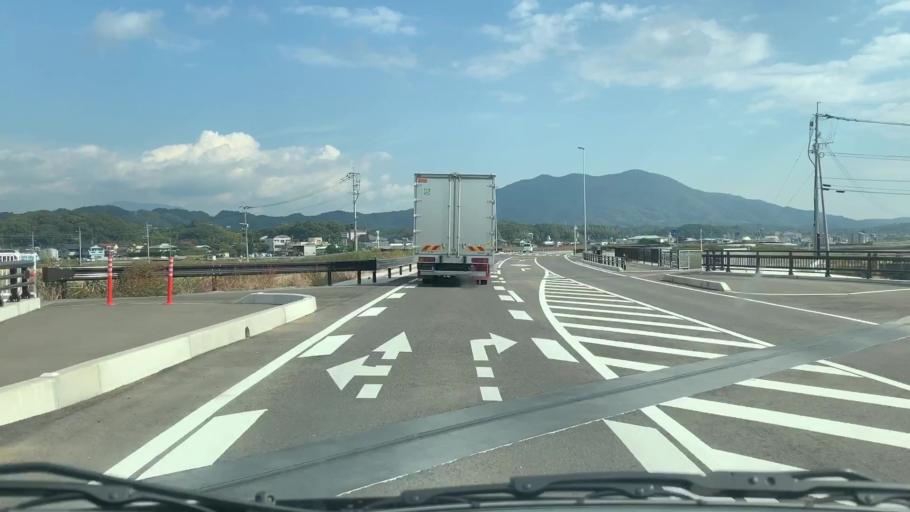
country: JP
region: Saga Prefecture
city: Takeocho-takeo
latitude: 33.2166
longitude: 130.0543
